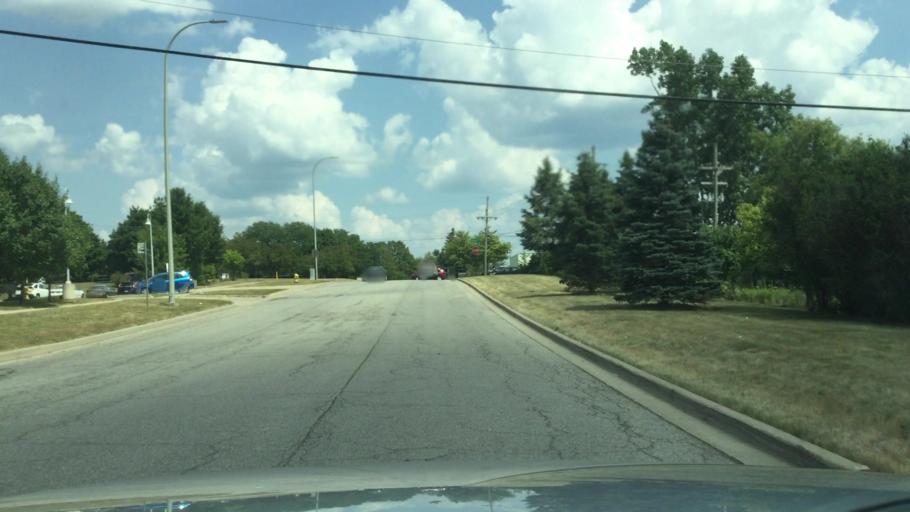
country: US
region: Michigan
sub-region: Washtenaw County
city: Ypsilanti
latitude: 42.2225
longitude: -83.6195
